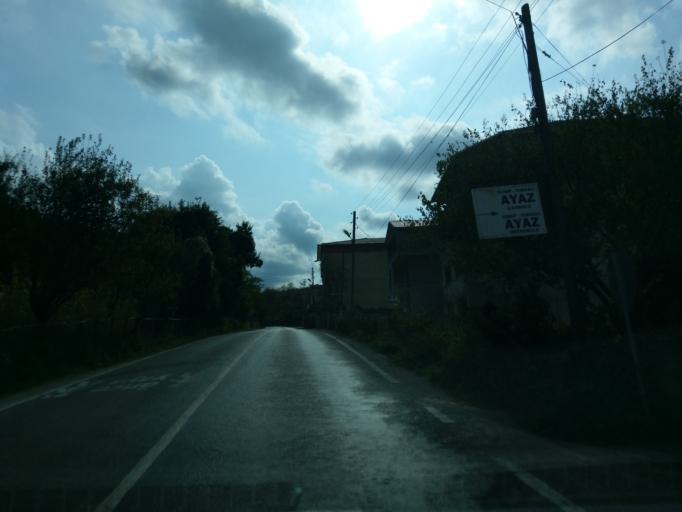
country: TR
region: Sinop
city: Helaldi
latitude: 41.9085
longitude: 34.4383
